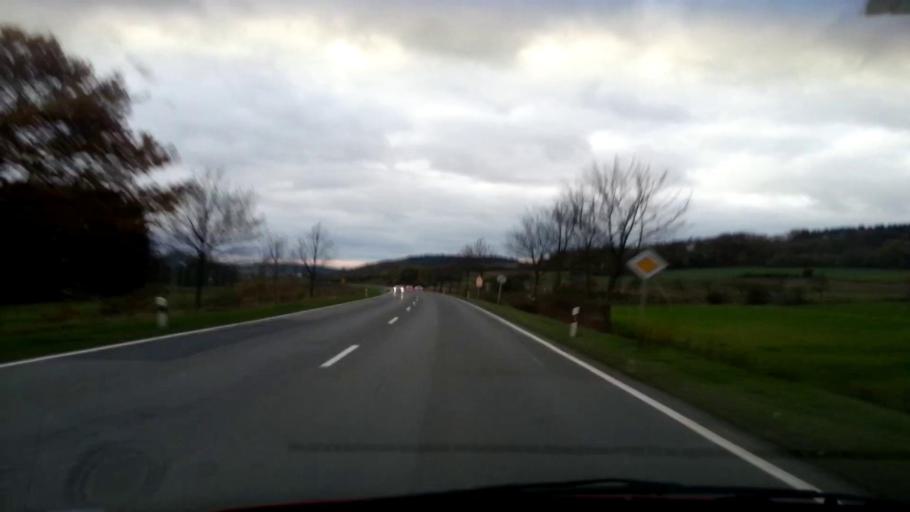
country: DE
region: Bavaria
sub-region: Upper Franconia
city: Kueps Oberfranken
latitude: 50.2128
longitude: 11.2408
